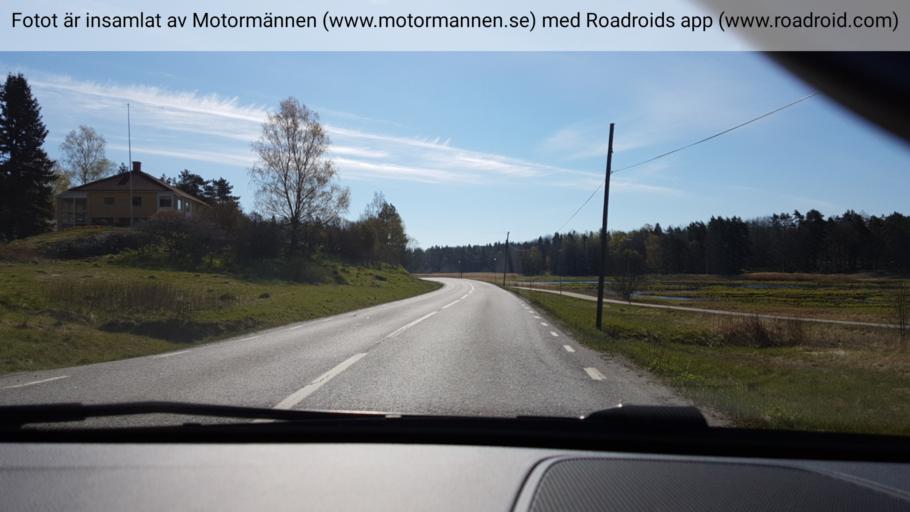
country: SE
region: Stockholm
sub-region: Varmdo Kommun
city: Hemmesta
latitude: 59.3271
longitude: 18.5100
